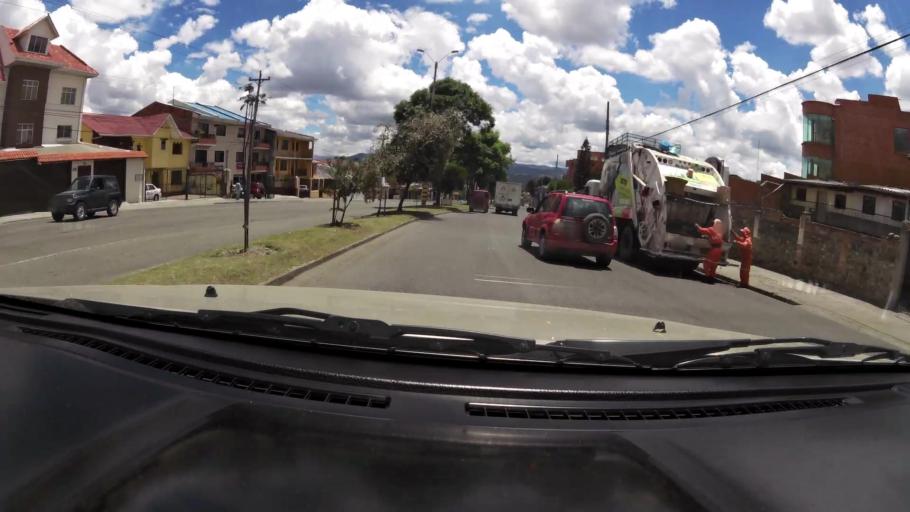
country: EC
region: Azuay
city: Cuenca
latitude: -2.8845
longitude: -79.0021
